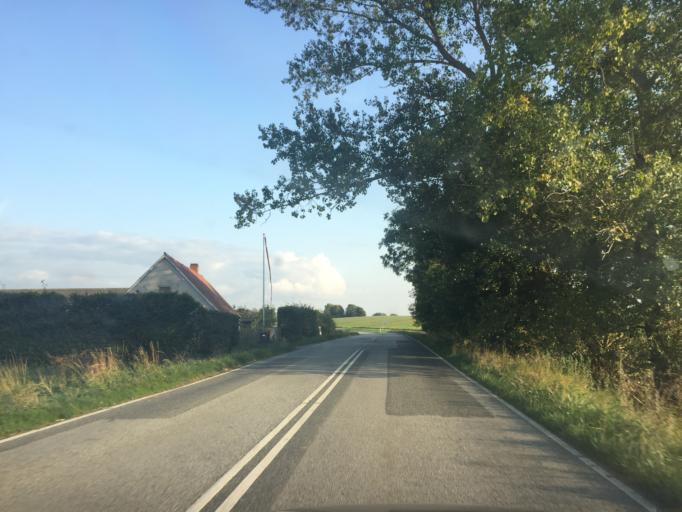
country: DK
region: Zealand
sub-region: Kalundborg Kommune
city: Svebolle
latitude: 55.6023
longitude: 11.2733
